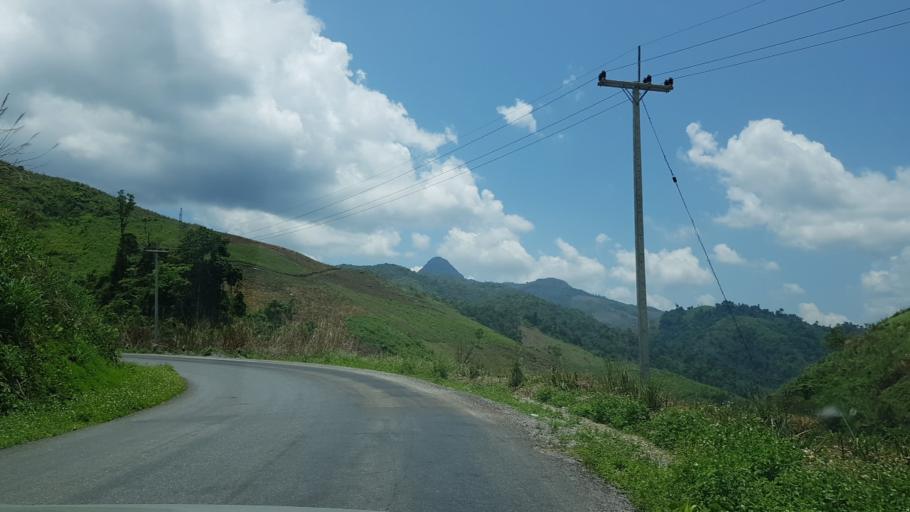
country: LA
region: Vientiane
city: Muang Kasi
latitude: 19.1399
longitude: 102.2919
